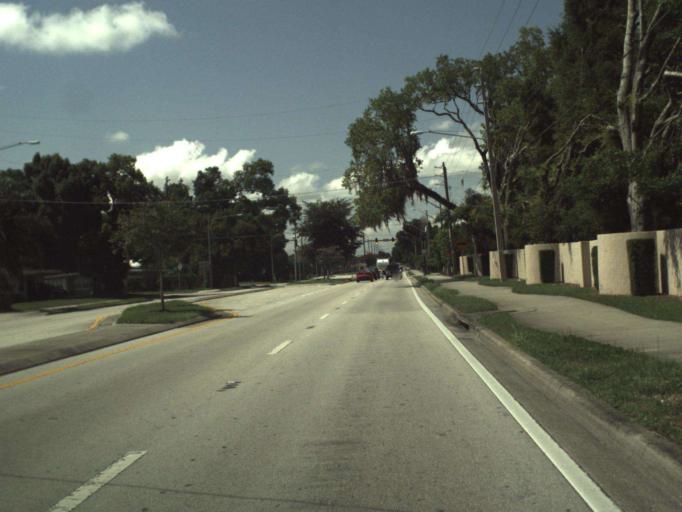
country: US
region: Florida
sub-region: Orange County
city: Conway
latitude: 28.5008
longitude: -81.3310
